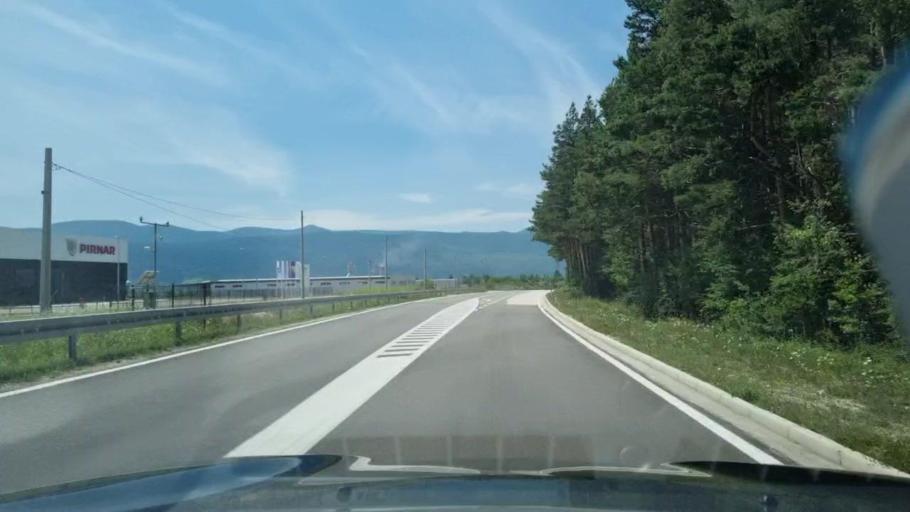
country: BA
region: Federation of Bosnia and Herzegovina
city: Sanica
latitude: 44.5386
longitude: 16.4014
